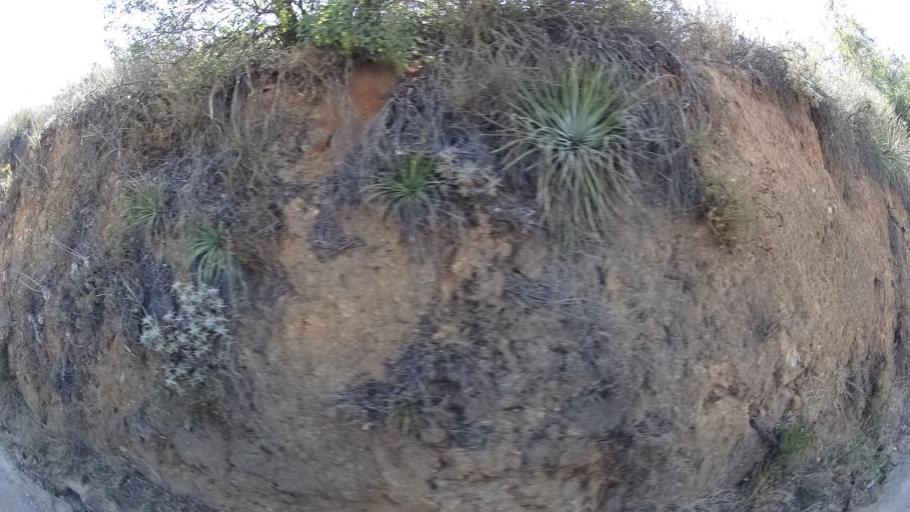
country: US
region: California
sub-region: San Diego County
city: Valley Center
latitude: 33.3267
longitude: -116.9673
